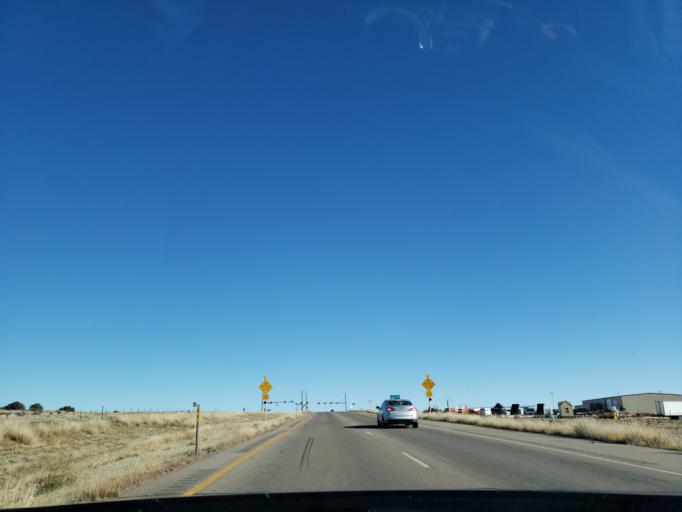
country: US
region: Colorado
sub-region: Fremont County
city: Florence
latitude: 38.4381
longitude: -105.1171
